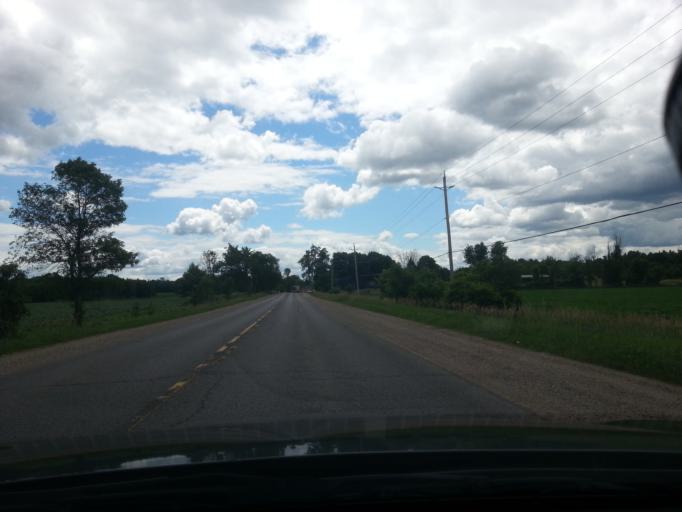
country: CA
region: Ontario
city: Perth
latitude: 44.6181
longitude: -76.2371
